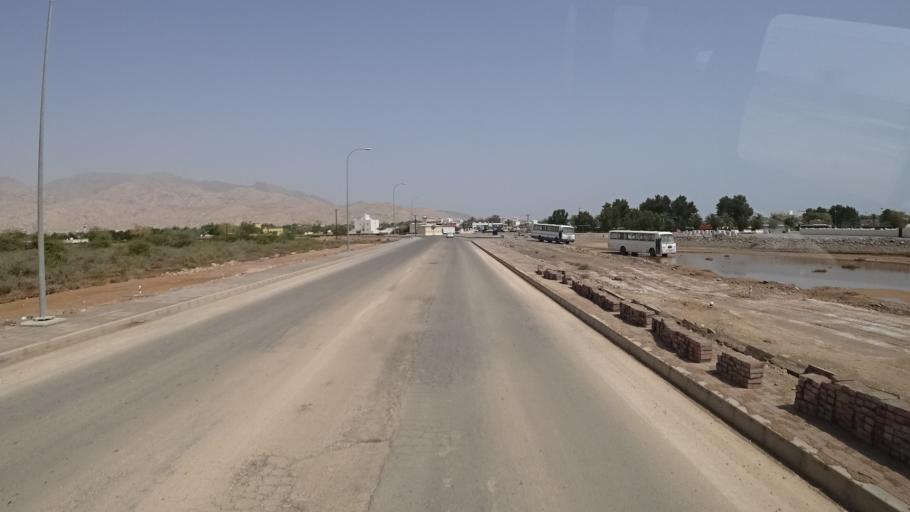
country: OM
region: Muhafazat Masqat
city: Muscat
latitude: 23.2527
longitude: 58.9106
